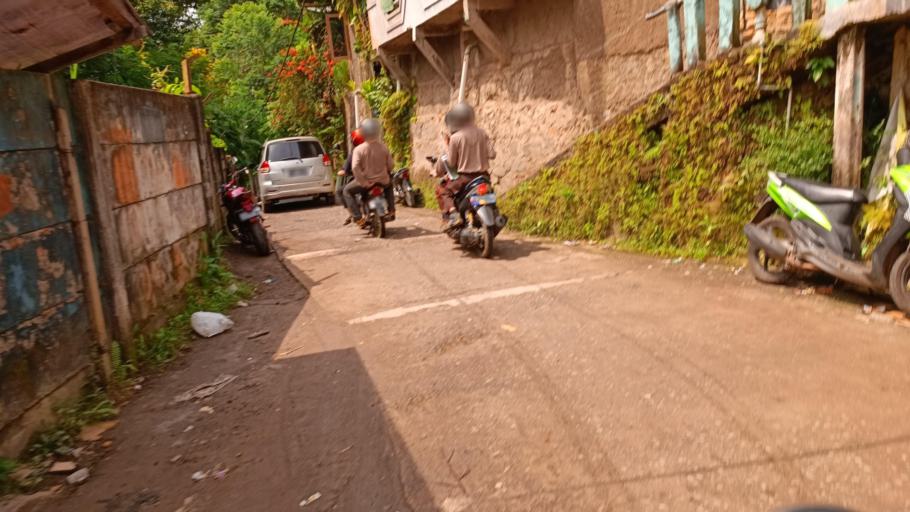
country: ID
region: West Java
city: Caringin
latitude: -6.6536
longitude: 106.8957
